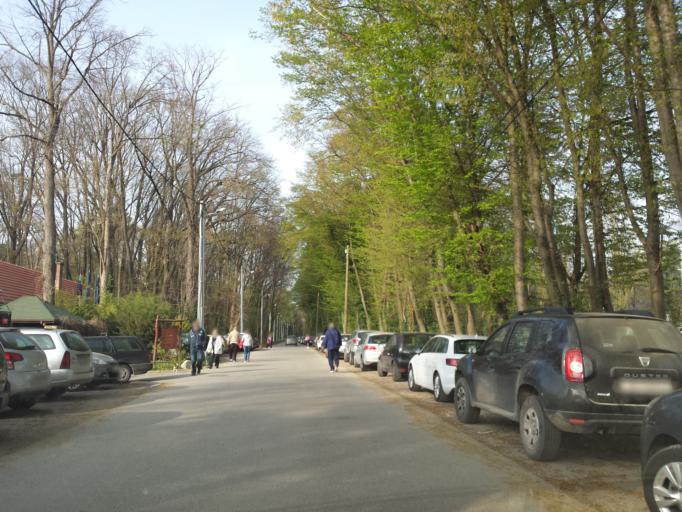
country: HR
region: Grad Zagreb
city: Dubrava
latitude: 45.8227
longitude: 16.0247
